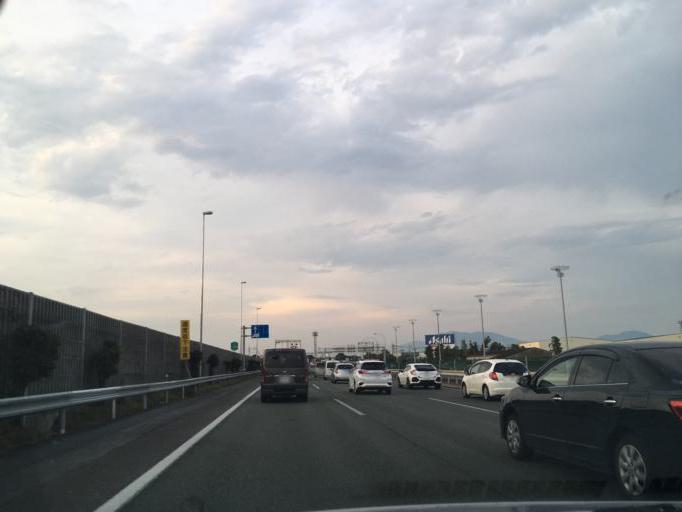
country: JP
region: Saga Prefecture
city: Tosu
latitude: 33.4031
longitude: 130.5380
